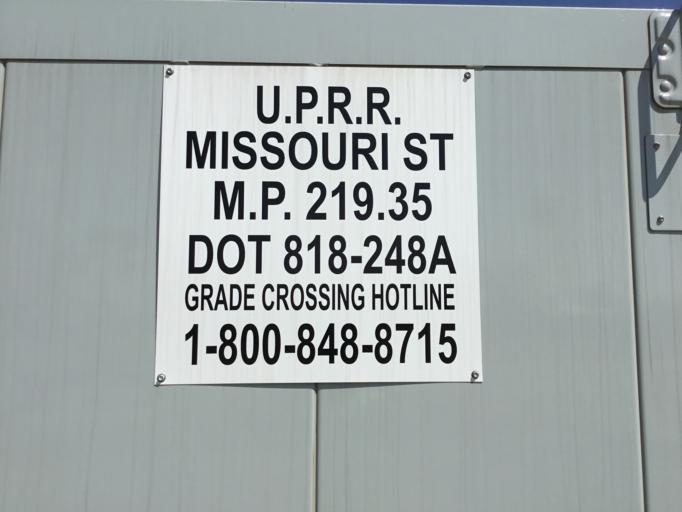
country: US
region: Kansas
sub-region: Ellsworth County
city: Ellsworth
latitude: 38.7150
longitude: -98.1562
